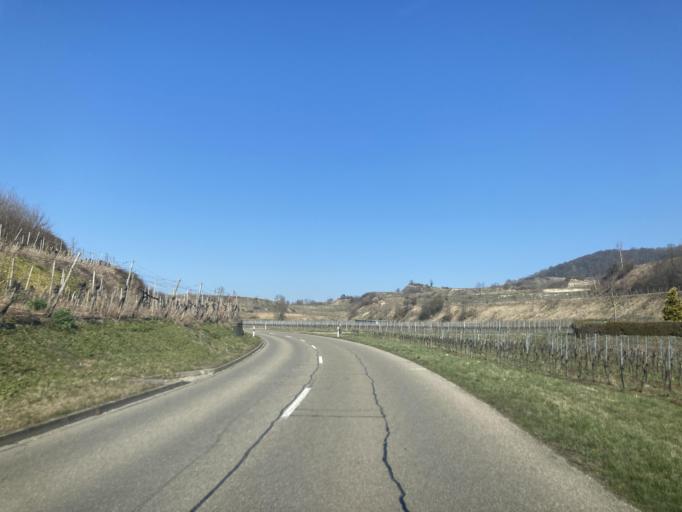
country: DE
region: Baden-Wuerttemberg
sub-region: Freiburg Region
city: Vogtsburg
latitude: 48.0939
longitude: 7.6276
